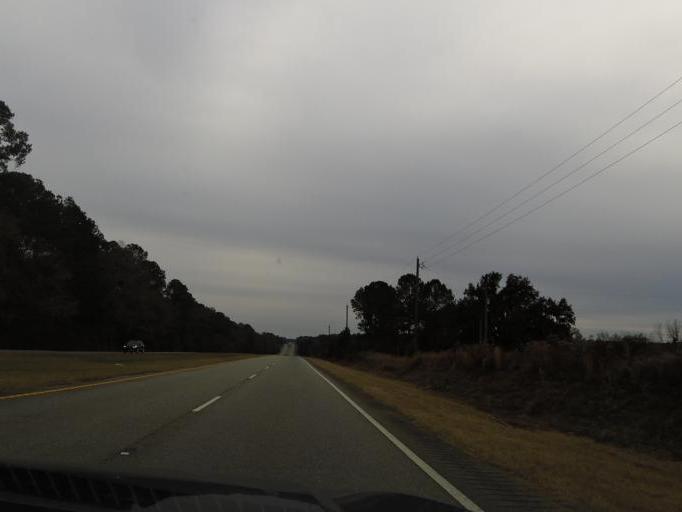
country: US
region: Georgia
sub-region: Thomas County
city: Boston
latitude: 30.7276
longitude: -83.8985
